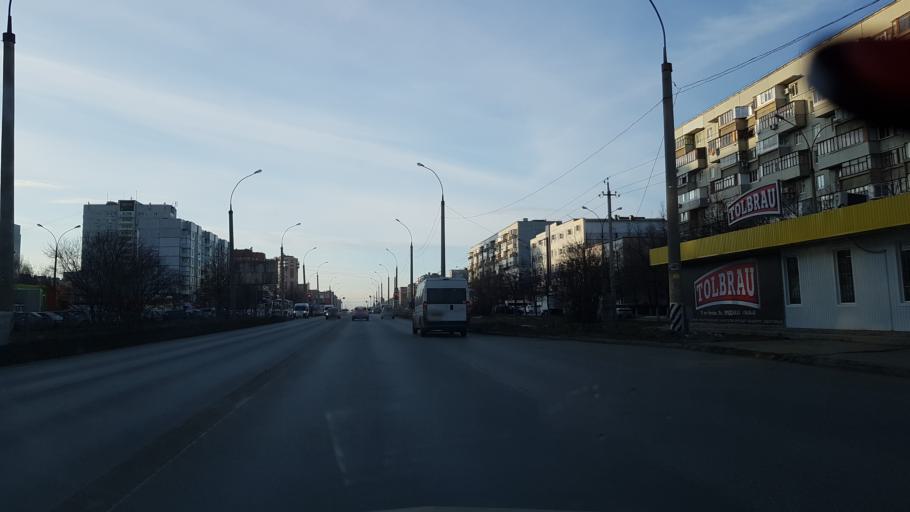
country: RU
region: Samara
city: Tol'yatti
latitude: 53.5406
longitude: 49.3513
